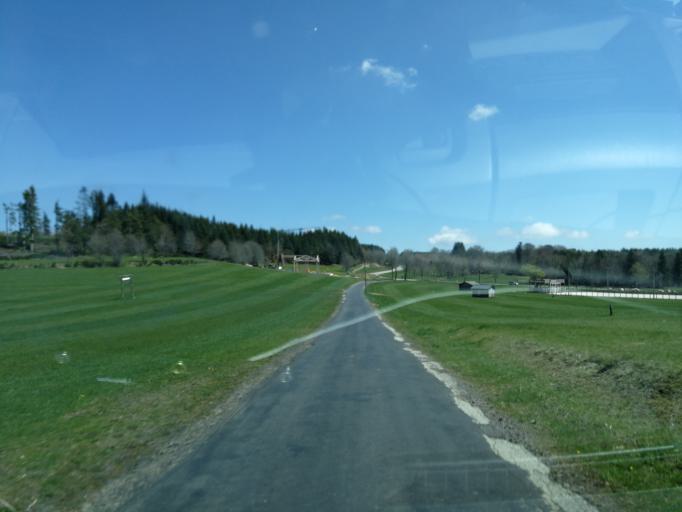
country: FR
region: Rhone-Alpes
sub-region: Departement de l'Ardeche
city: Saint-Agreve
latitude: 45.0158
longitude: 4.3998
